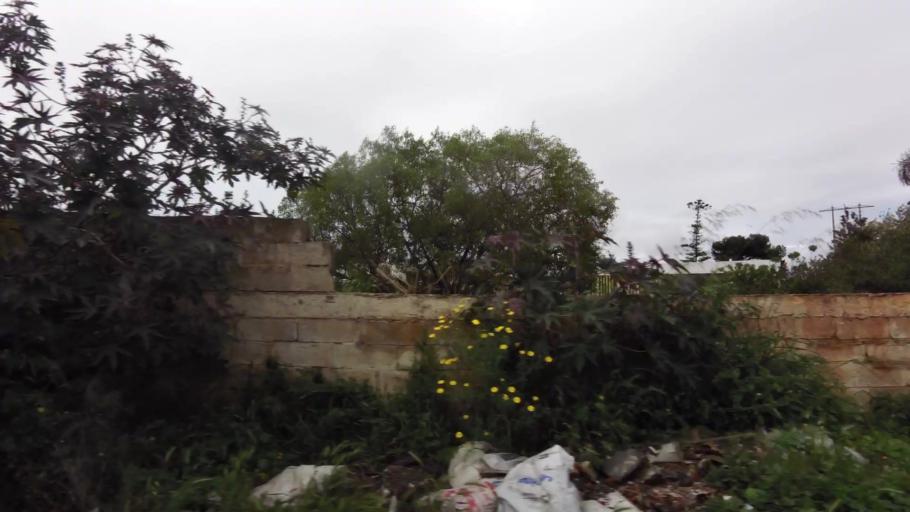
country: MA
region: Grand Casablanca
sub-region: Casablanca
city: Casablanca
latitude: 33.5322
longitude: -7.6454
